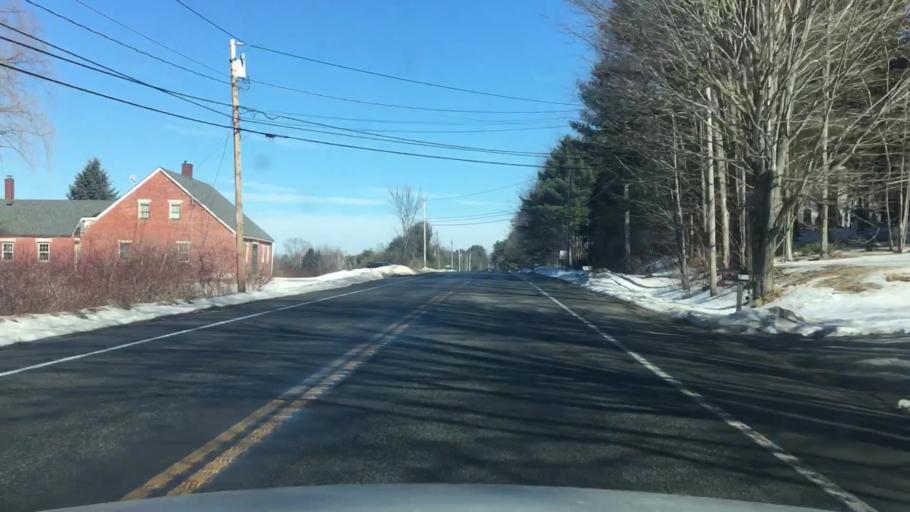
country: US
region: Maine
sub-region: Cumberland County
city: North Windham
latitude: 43.8258
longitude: -70.3877
